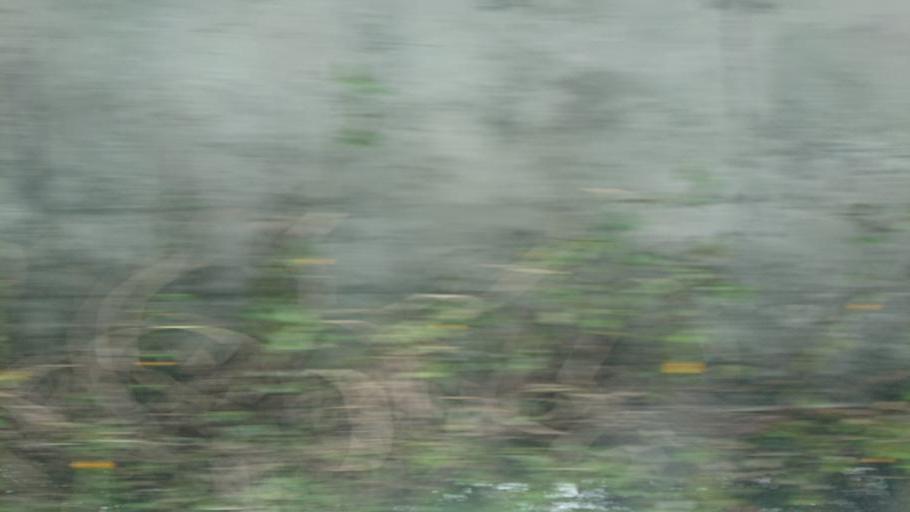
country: TW
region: Taipei
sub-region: Taipei
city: Banqiao
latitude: 24.9795
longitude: 121.5228
